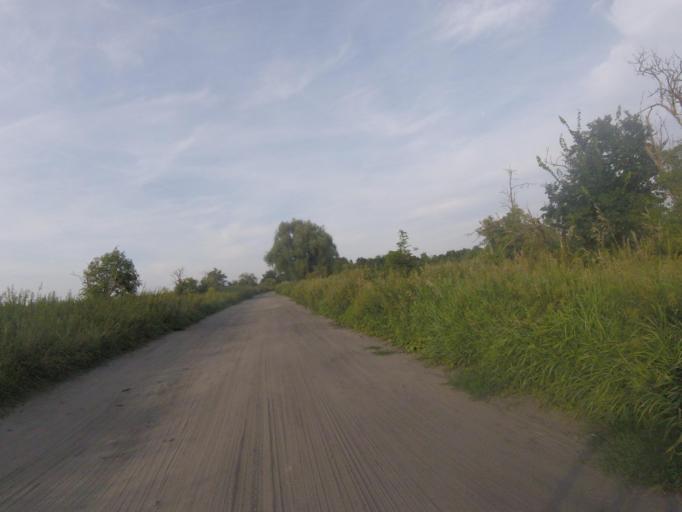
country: DE
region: Berlin
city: Gropiusstadt
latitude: 52.3822
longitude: 13.4496
